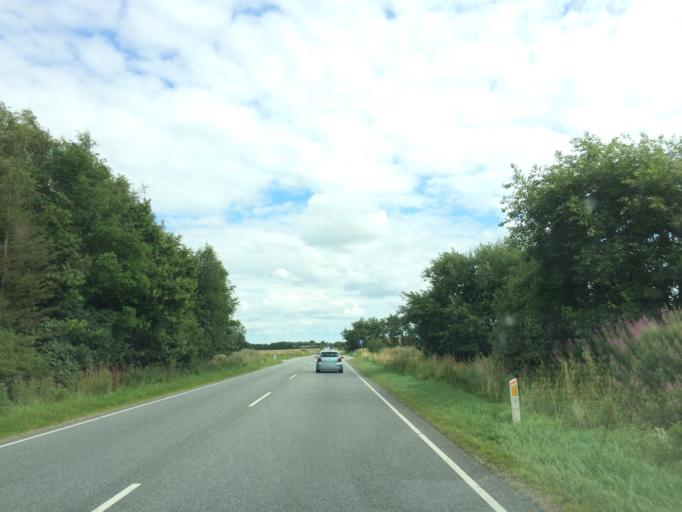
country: DK
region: Central Jutland
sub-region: Favrskov Kommune
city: Hammel
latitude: 56.2622
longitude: 9.7459
